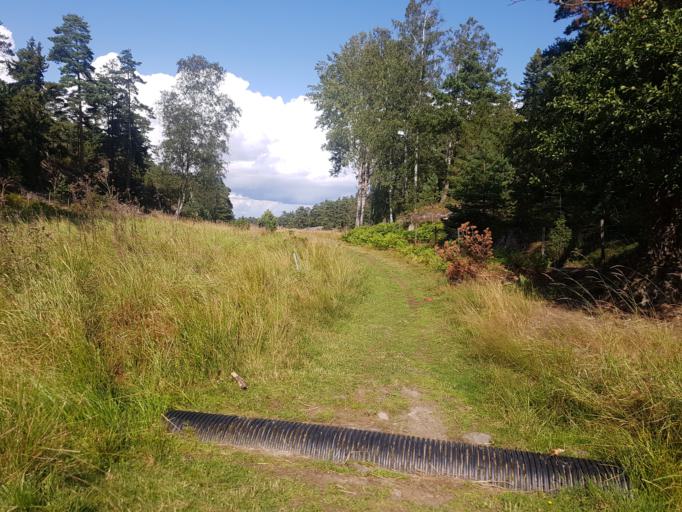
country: SE
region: Stockholm
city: Dalaro
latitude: 59.0458
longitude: 18.5207
